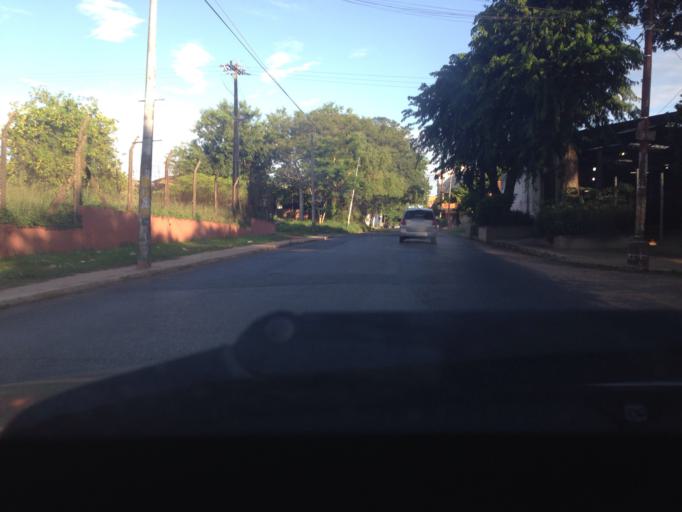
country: PY
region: Central
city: Lambare
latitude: -25.3207
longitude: -57.5874
